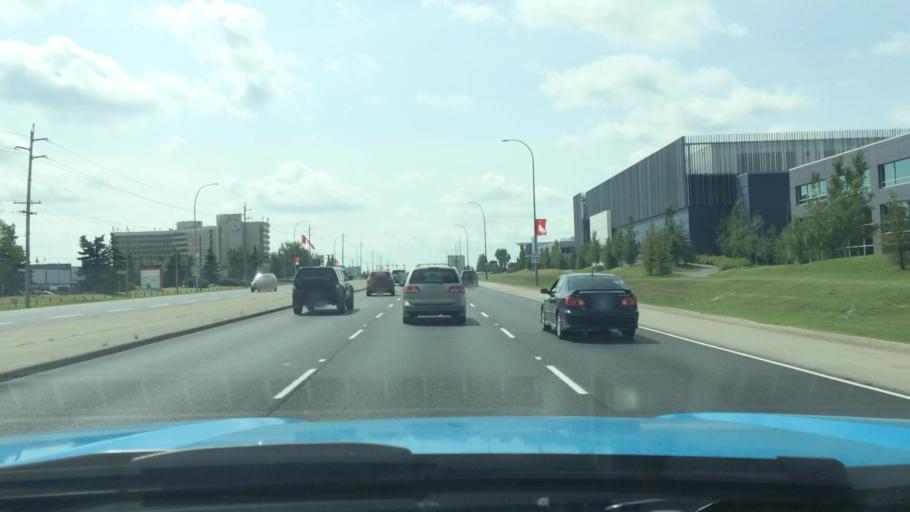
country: CA
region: Alberta
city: Calgary
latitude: 51.0857
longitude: -114.0019
